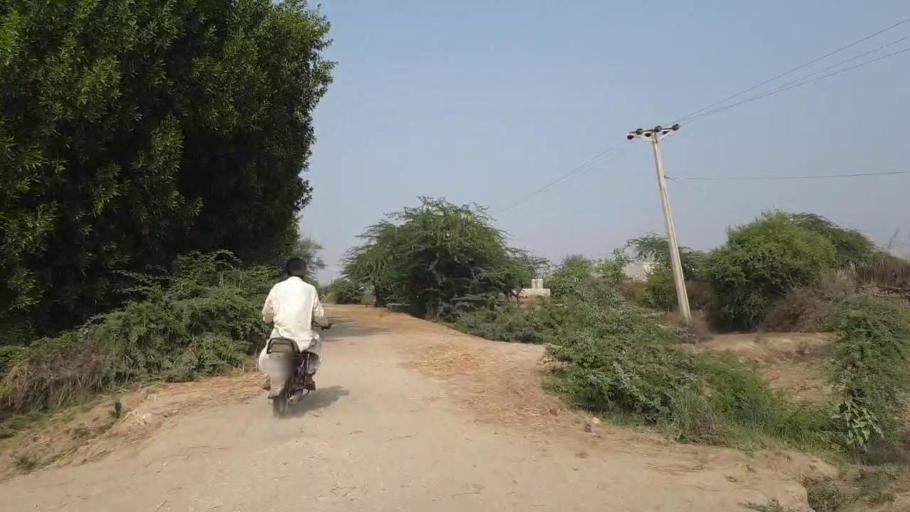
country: PK
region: Sindh
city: Kario
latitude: 24.9284
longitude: 68.6010
